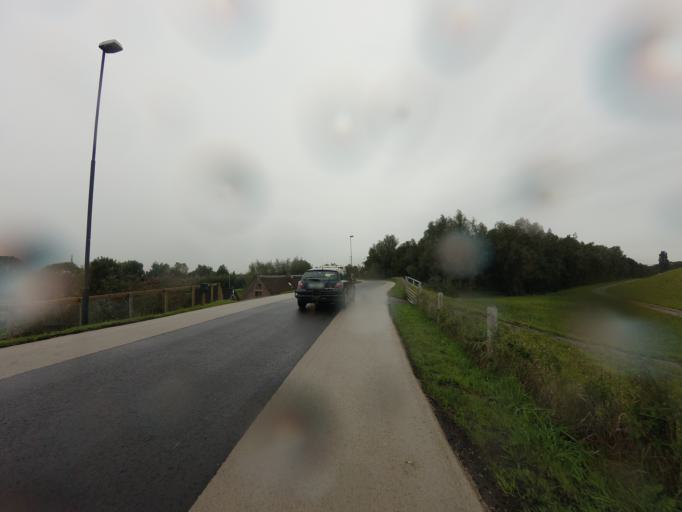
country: NL
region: South Holland
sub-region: Molenwaard
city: Liesveld
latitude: 51.9297
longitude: 4.8293
